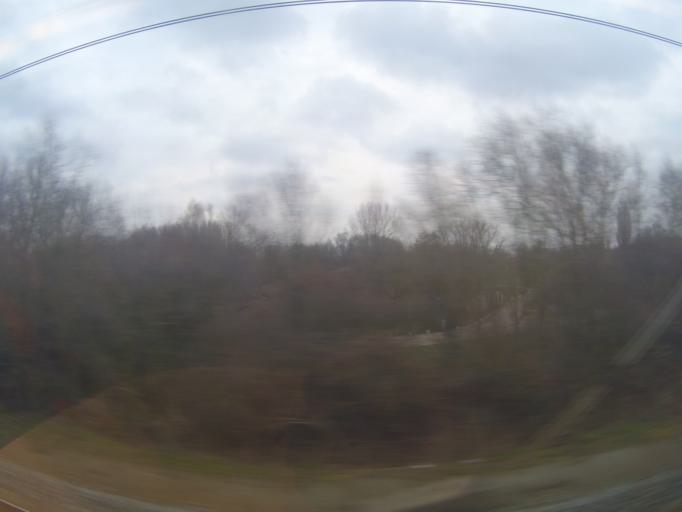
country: NL
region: Utrecht
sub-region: Gemeente Utrecht
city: Utrecht
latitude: 52.1131
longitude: 5.1386
